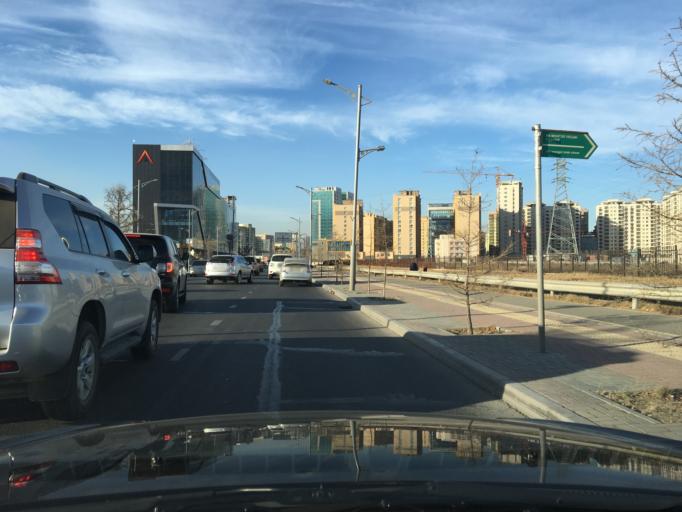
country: MN
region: Ulaanbaatar
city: Ulaanbaatar
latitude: 47.8976
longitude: 106.9328
